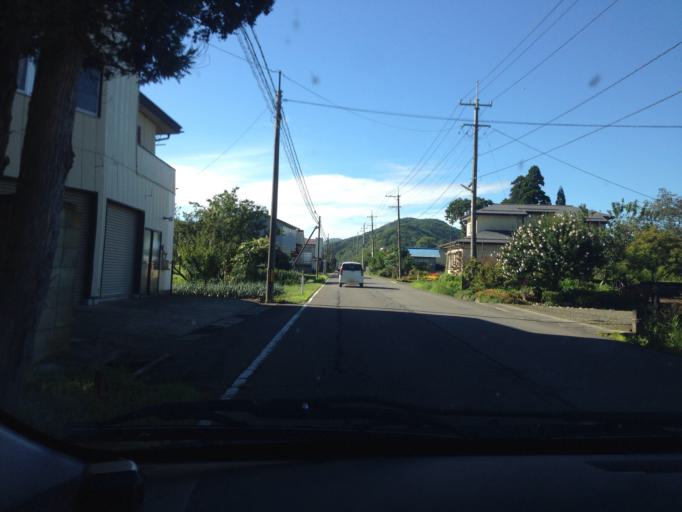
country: JP
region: Fukushima
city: Inawashiro
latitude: 37.4018
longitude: 140.1293
